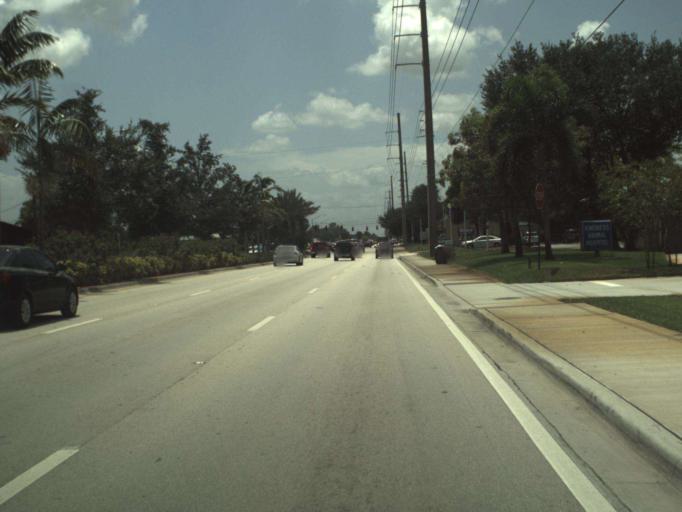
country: US
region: Florida
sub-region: Saint Lucie County
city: Port Saint Lucie
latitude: 27.2720
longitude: -80.3288
